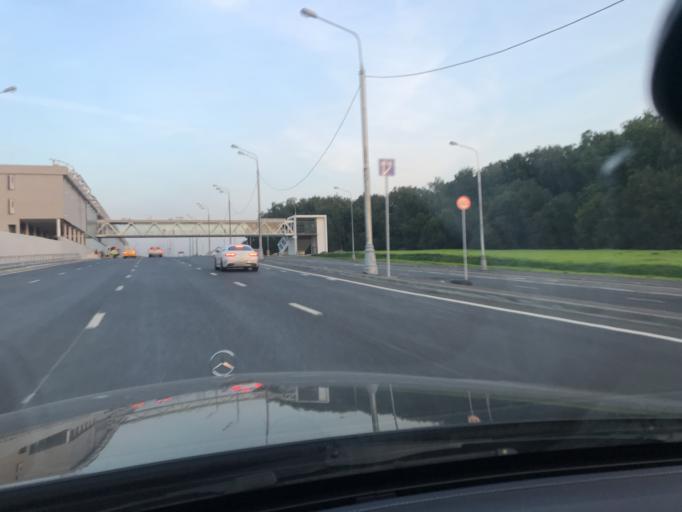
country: RU
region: Moskovskaya
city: Mosrentgen
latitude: 55.5873
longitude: 37.4306
